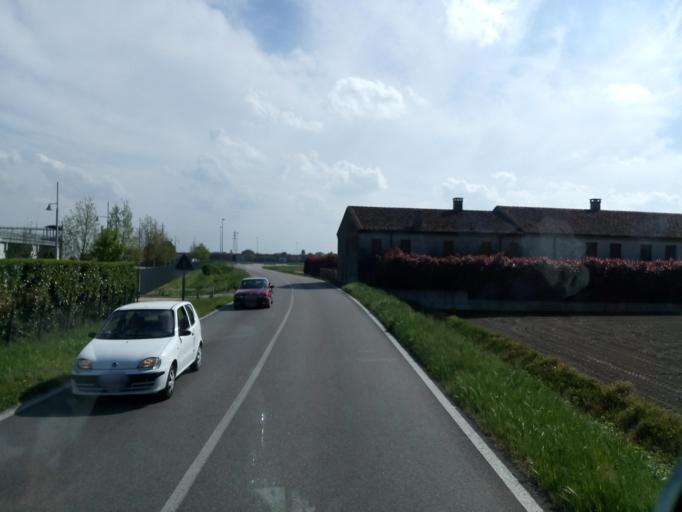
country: IT
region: Veneto
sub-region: Provincia di Verona
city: Boschi Sant'Anna
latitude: 45.2116
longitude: 11.3197
